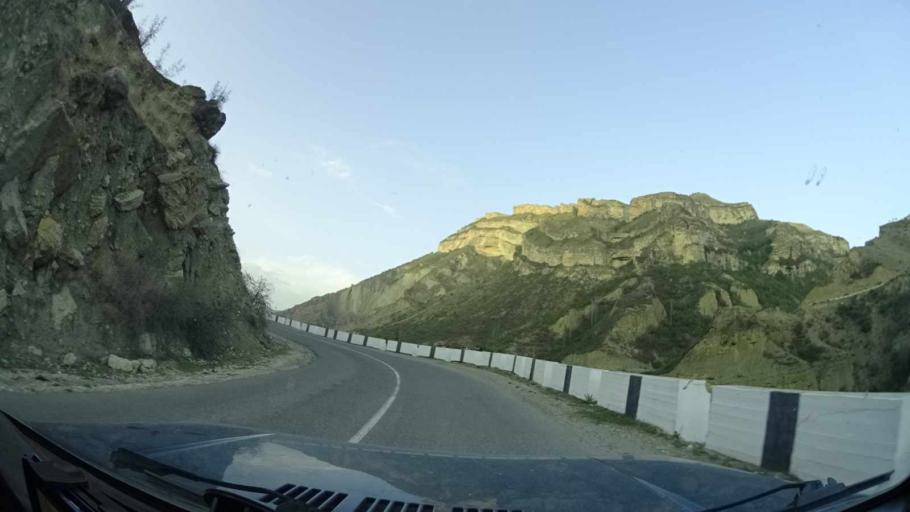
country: RU
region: Dagestan
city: Gunib
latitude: 42.3837
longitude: 46.9681
